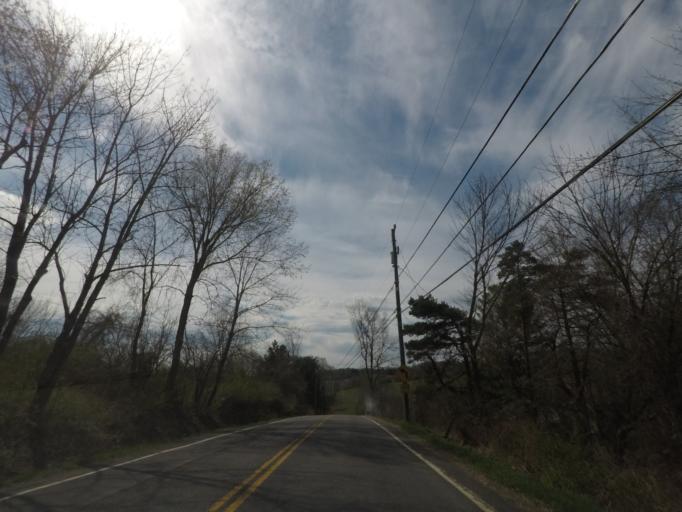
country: US
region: New York
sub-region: Columbia County
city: Chatham
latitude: 42.3561
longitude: -73.5491
